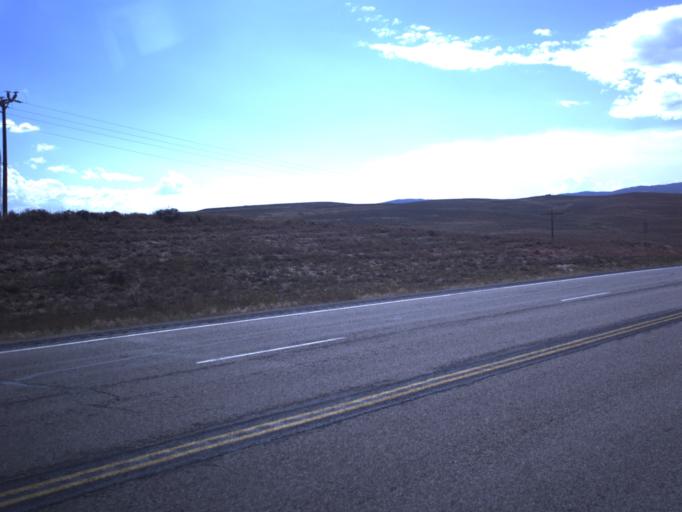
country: US
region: Utah
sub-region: Wasatch County
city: Heber
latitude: 40.1851
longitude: -111.0599
